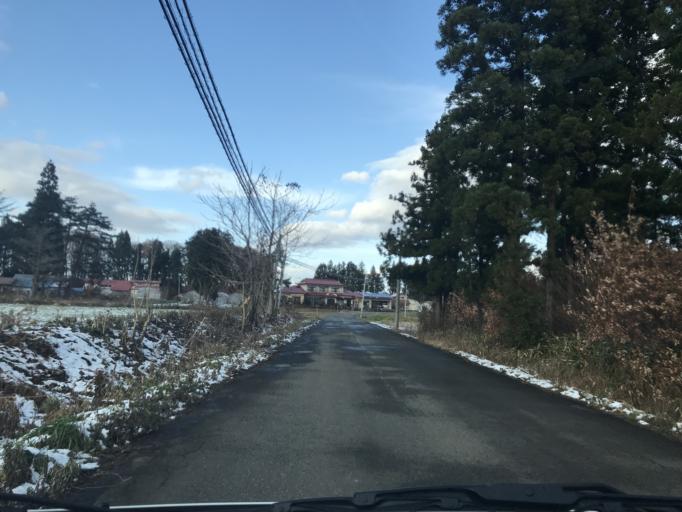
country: JP
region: Iwate
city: Kitakami
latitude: 39.2249
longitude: 141.0451
